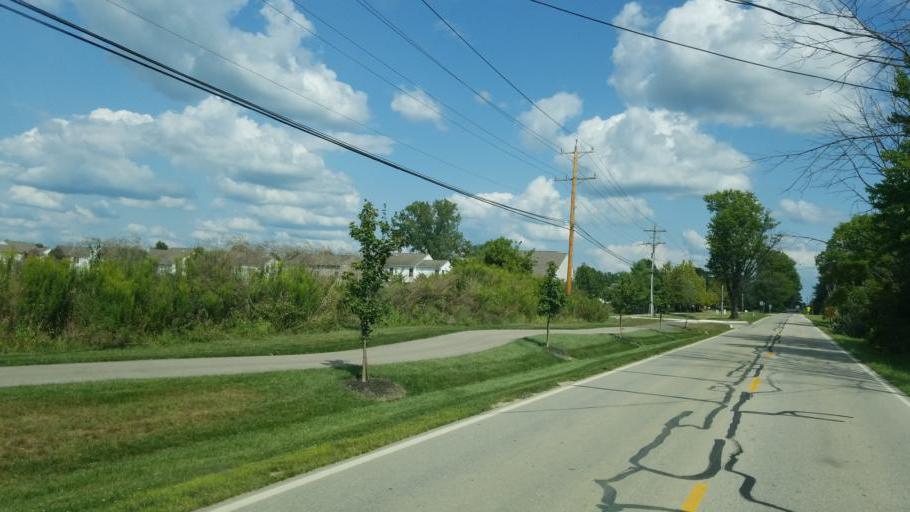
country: US
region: Ohio
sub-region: Delaware County
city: Lewis Center
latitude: 40.2419
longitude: -83.0477
